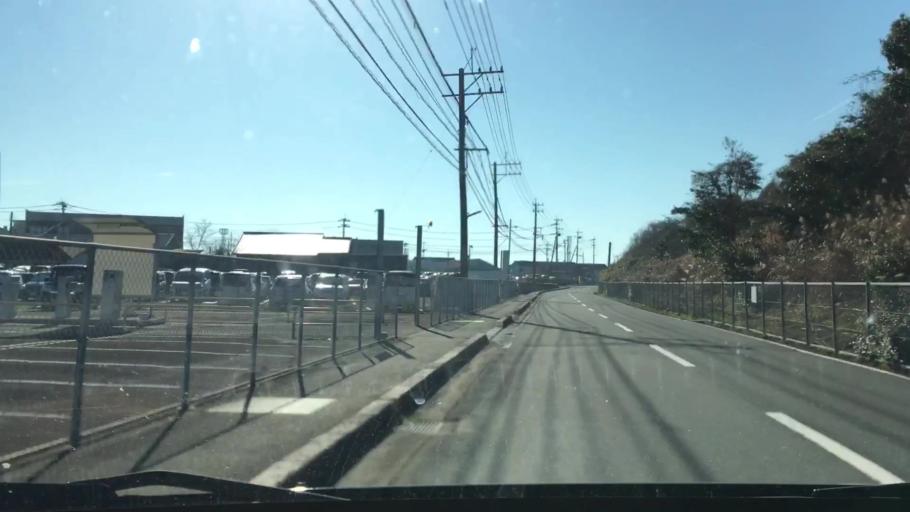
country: JP
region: Kagoshima
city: Kajiki
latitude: 31.7962
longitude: 130.7157
